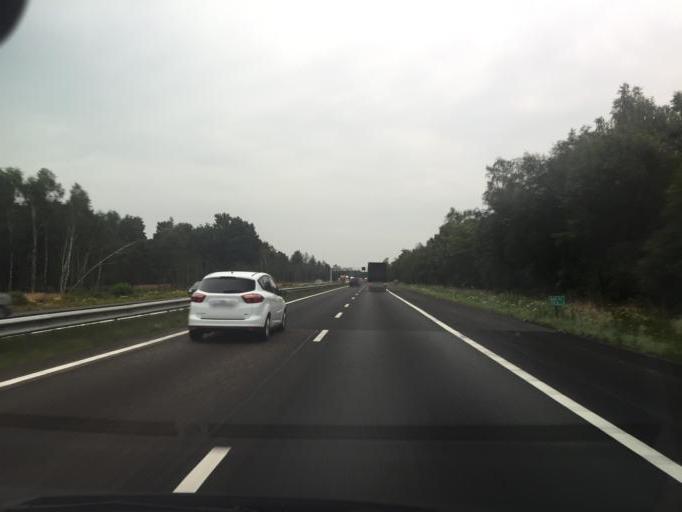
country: NL
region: North Brabant
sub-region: Gemeente Geldrop-Mierlo
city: Geldrop
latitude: 51.4144
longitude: 5.5850
